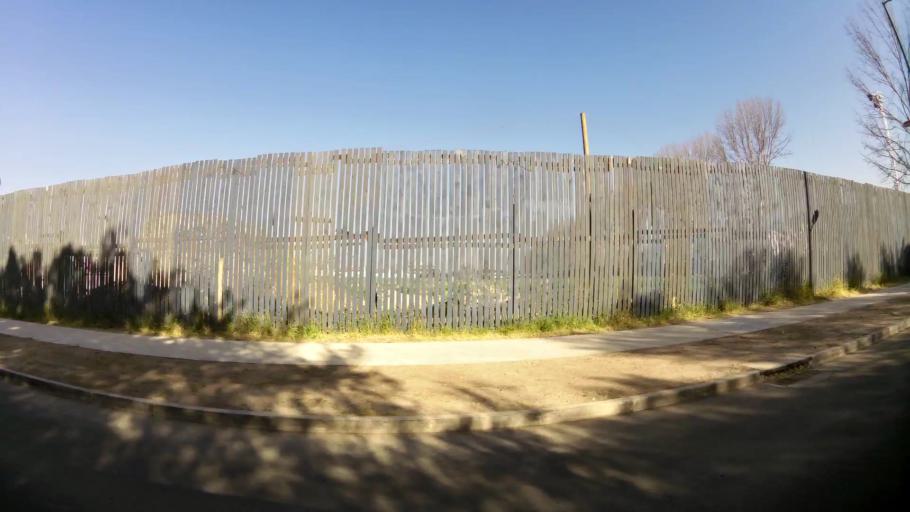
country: CL
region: Santiago Metropolitan
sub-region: Provincia de Chacabuco
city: Chicureo Abajo
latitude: -33.3621
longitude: -70.6645
